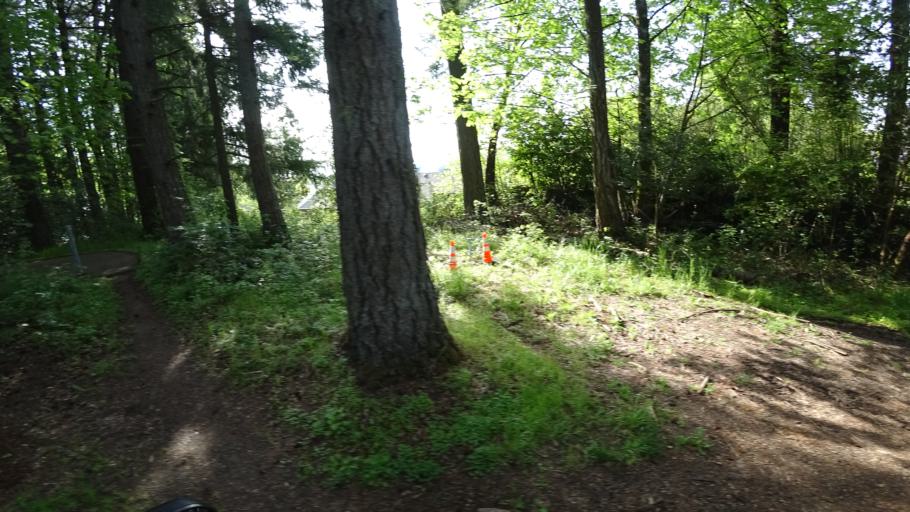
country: US
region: Oregon
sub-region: Washington County
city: King City
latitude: 45.4346
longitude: -122.8468
